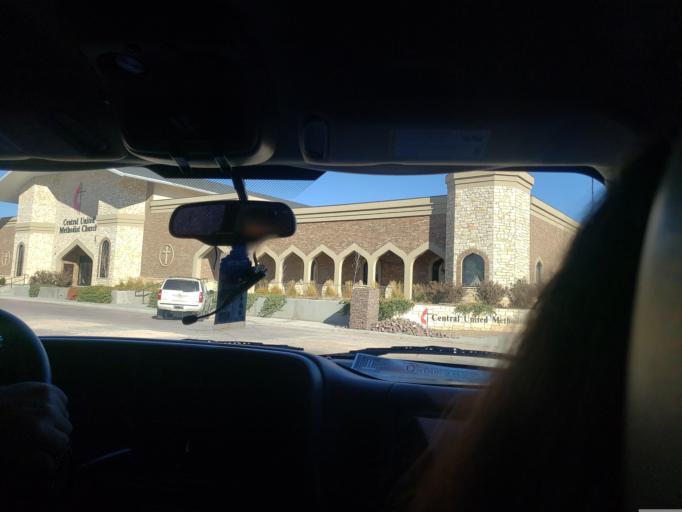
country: US
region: Texas
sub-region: Dallam County
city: Dalhart
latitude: 36.0595
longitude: -102.5245
